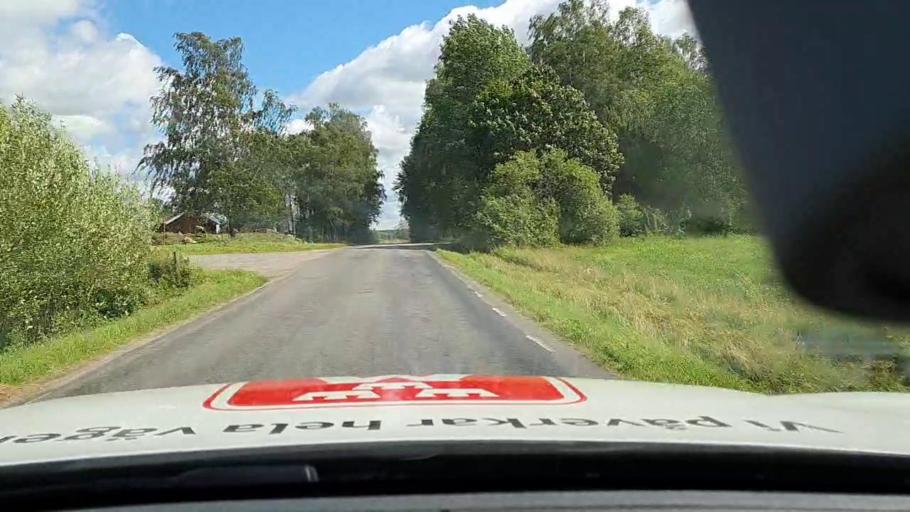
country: SE
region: Vaestra Goetaland
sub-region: Toreboda Kommun
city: Toereboda
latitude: 58.5712
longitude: 14.0655
